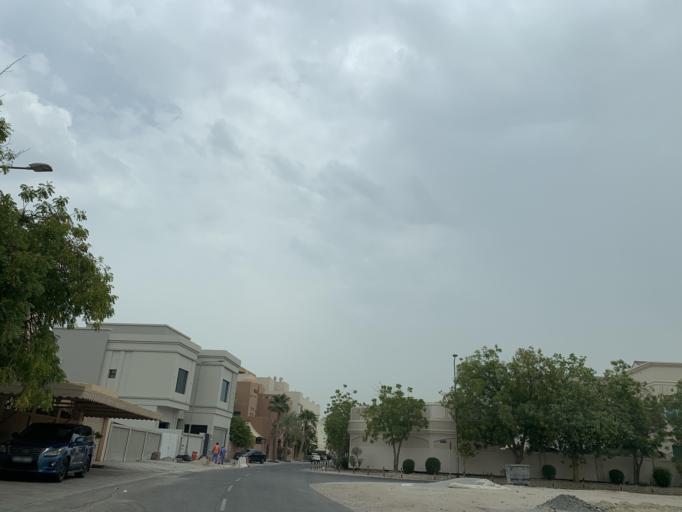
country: BH
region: Northern
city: Madinat `Isa
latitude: 26.1886
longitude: 50.4756
